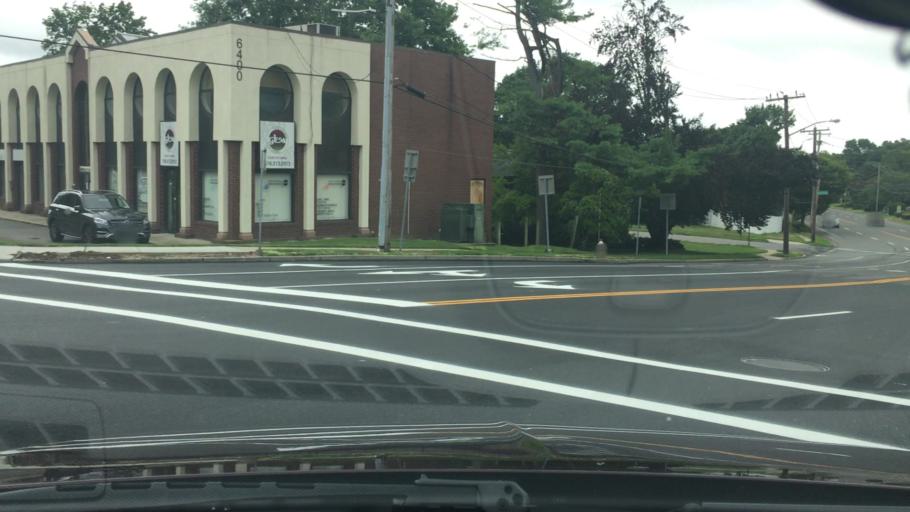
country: US
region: New York
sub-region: Nassau County
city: Jericho
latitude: 40.8026
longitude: -73.5282
